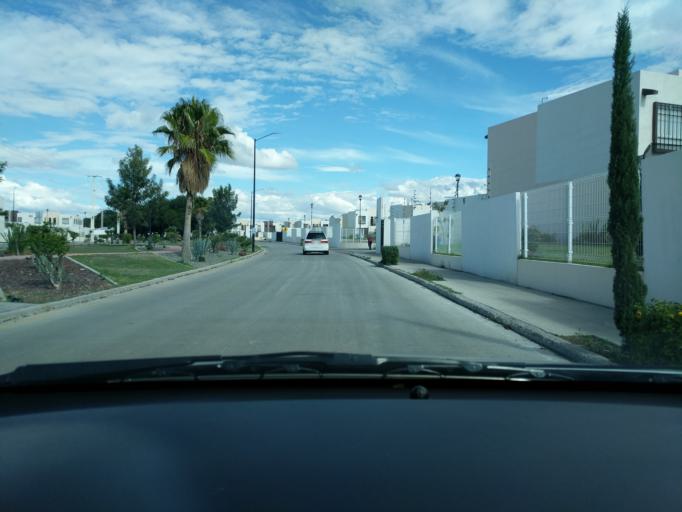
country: MX
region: Queretaro
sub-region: El Marques
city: La Loma
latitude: 20.5859
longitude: -100.2581
